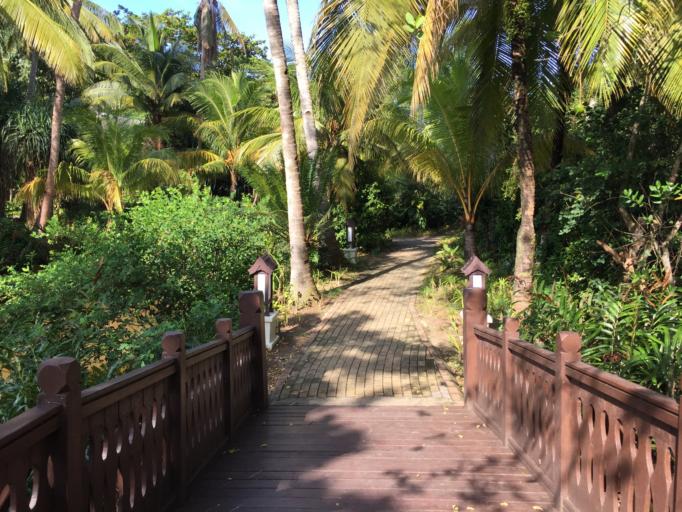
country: MY
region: Terengganu
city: Paka
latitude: 4.8118
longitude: 103.4233
